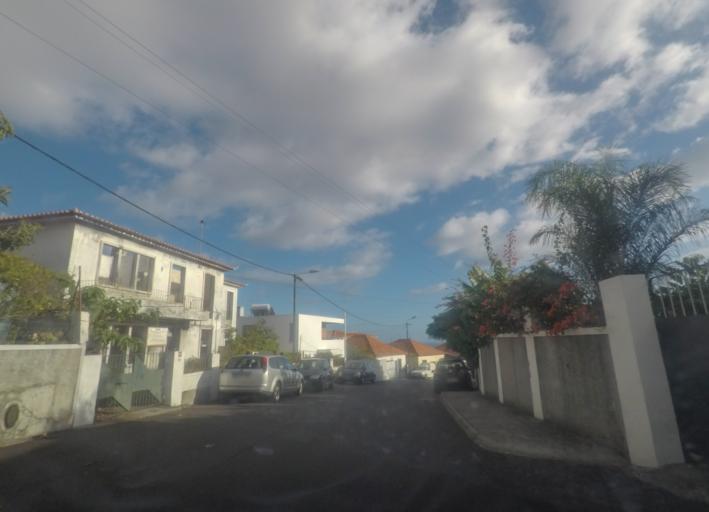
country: PT
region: Madeira
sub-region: Funchal
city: Nossa Senhora do Monte
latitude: 32.6565
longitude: -16.9019
